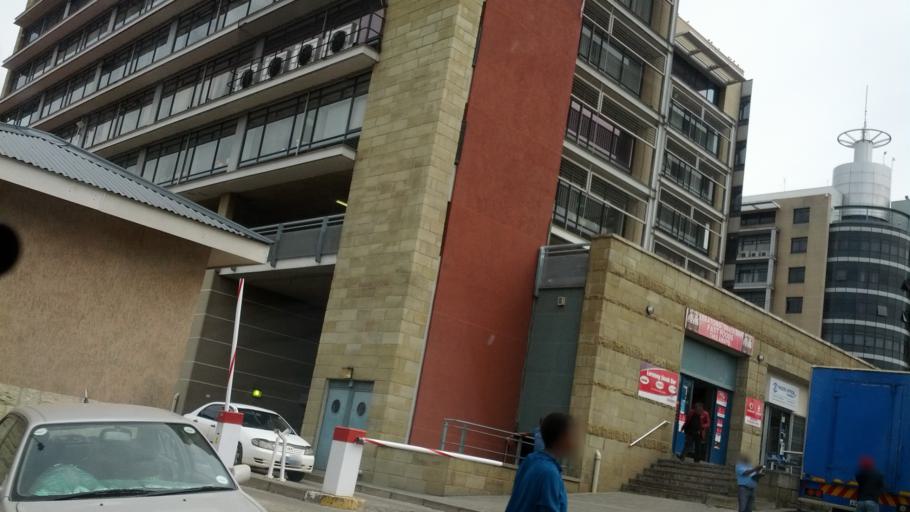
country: LS
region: Maseru
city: Maseru
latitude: -29.3145
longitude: 27.4824
